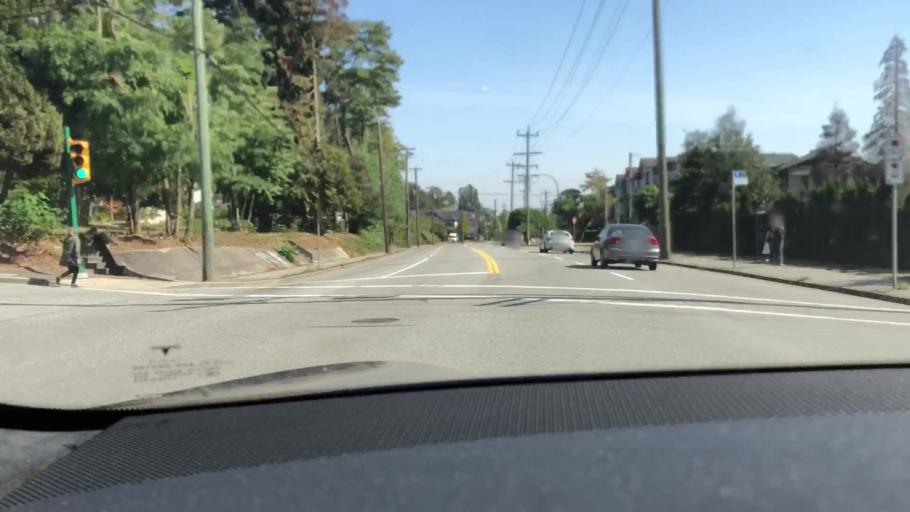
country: CA
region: British Columbia
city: New Westminster
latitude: 49.2174
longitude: -122.9458
